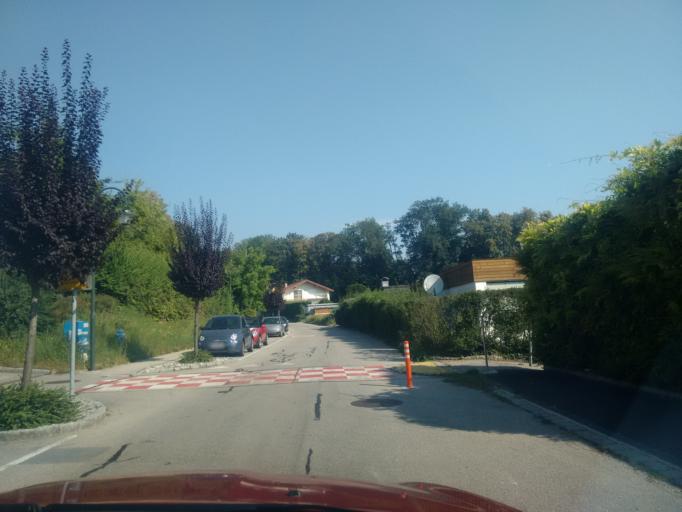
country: AT
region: Upper Austria
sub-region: Wels-Land
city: Thalheim bei Wels
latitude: 48.1488
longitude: 14.0407
